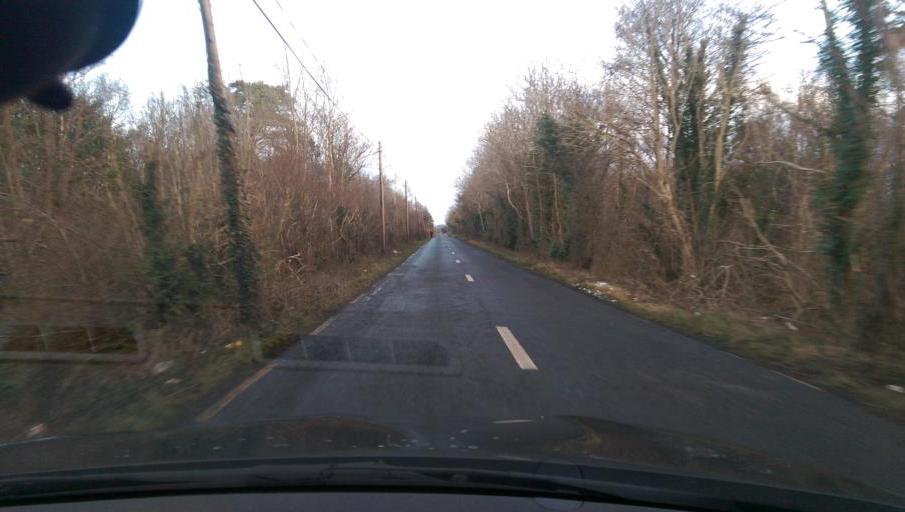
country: IE
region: Connaught
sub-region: County Galway
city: Ballinasloe
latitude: 53.3598
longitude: -8.2576
